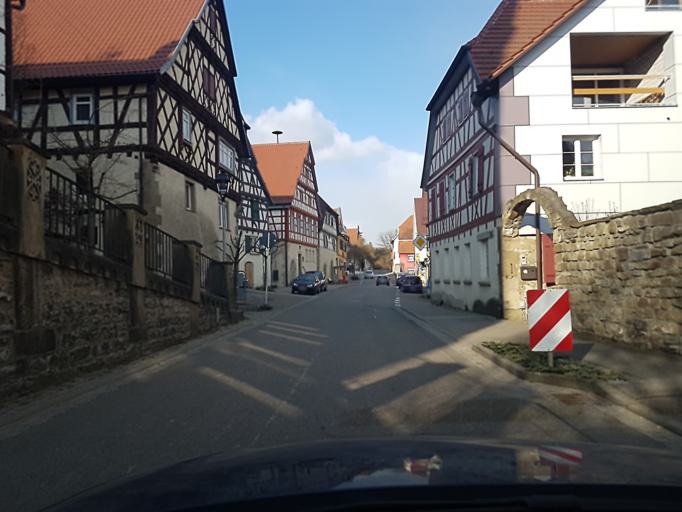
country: DE
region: Baden-Wuerttemberg
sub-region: Regierungsbezirk Stuttgart
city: Oberriexingen
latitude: 48.9258
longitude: 9.0285
